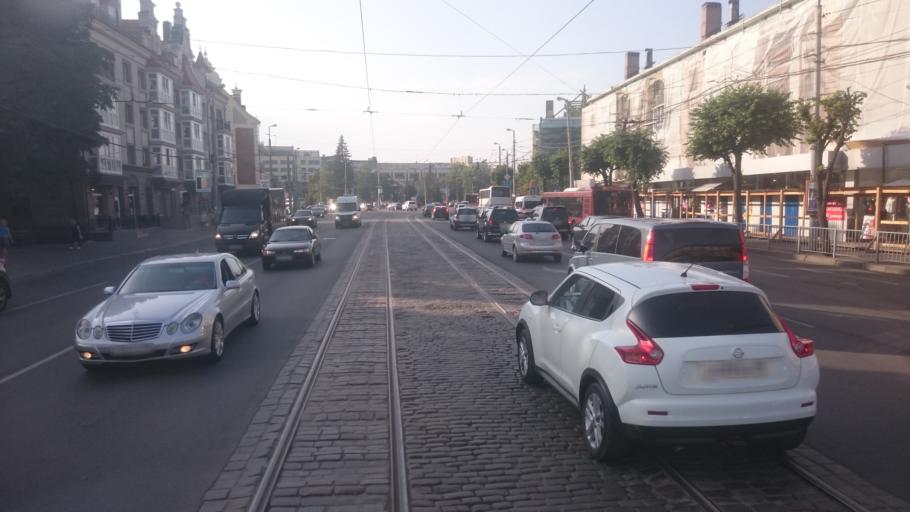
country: RU
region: Kaliningrad
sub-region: Gorod Kaliningrad
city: Kaliningrad
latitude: 54.7153
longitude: 20.5040
